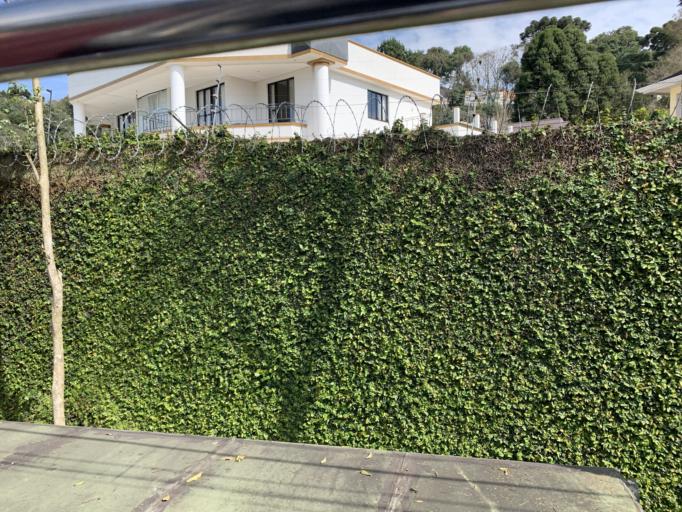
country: BR
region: Parana
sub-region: Curitiba
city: Curitiba
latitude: -25.4024
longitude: -49.3057
